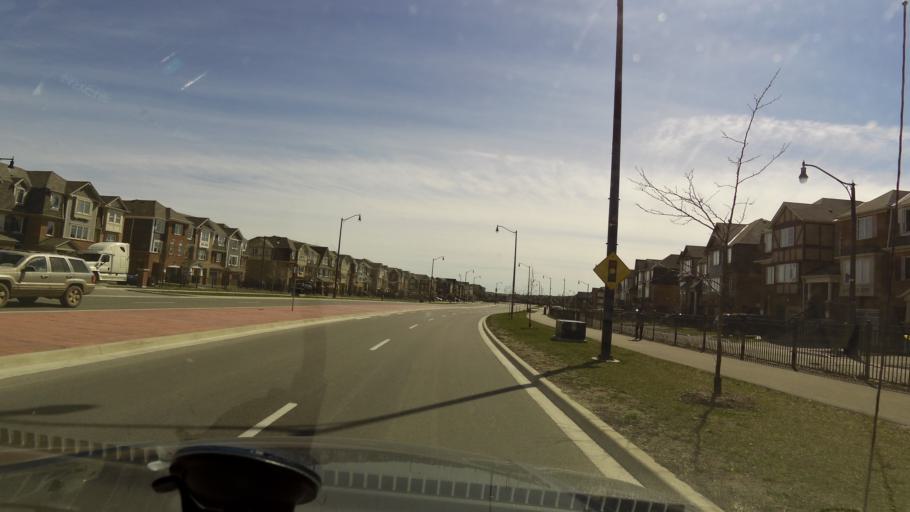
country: CA
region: Ontario
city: Brampton
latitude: 43.6811
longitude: -79.8275
